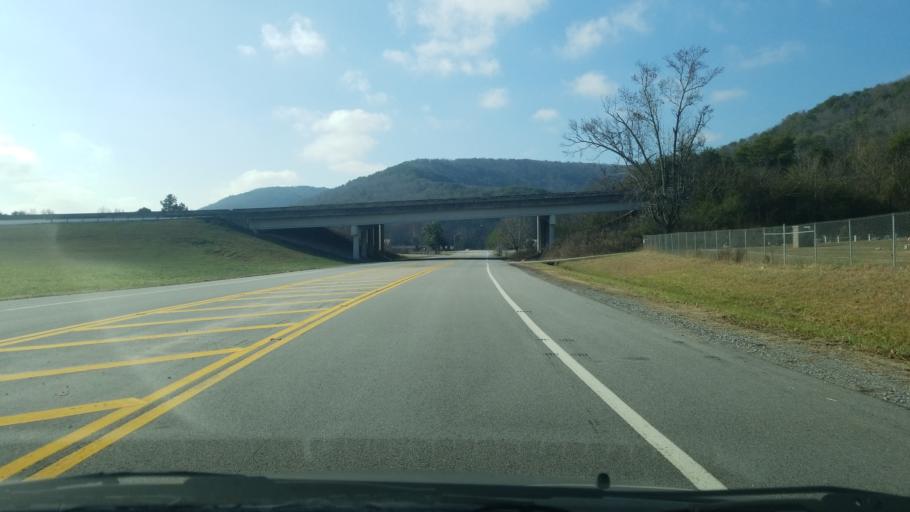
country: US
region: Tennessee
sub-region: Hamilton County
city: Soddy-Daisy
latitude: 35.3054
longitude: -85.1618
